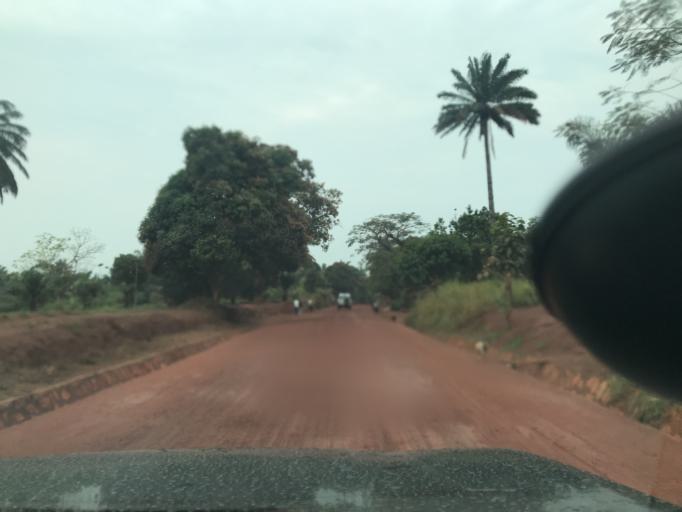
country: CD
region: Equateur
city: Gemena
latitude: 3.2309
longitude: 19.7780
